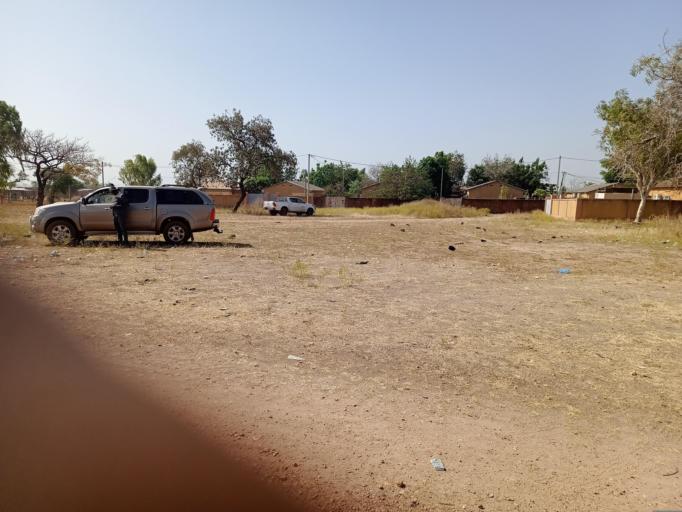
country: BF
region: Centre-Est
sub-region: Province du Boulgou
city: Garango
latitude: 11.4824
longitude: -0.5308
